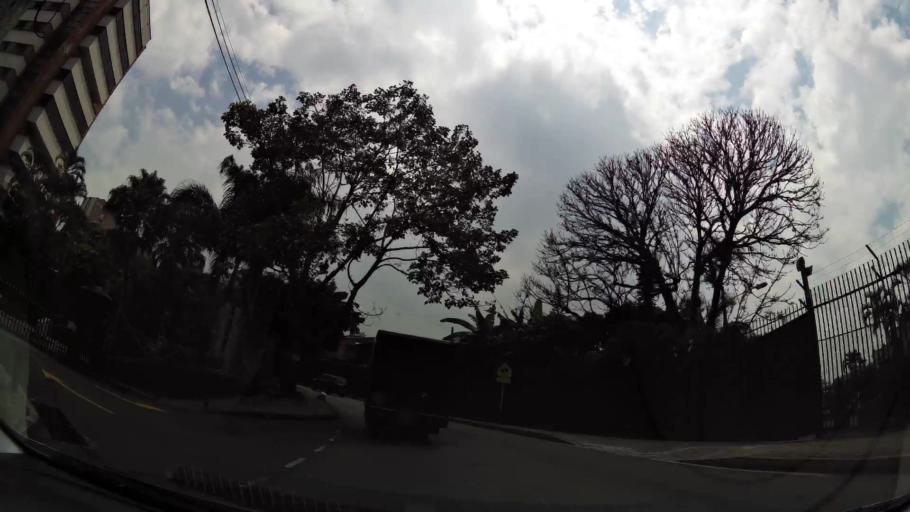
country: CO
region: Antioquia
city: Envigado
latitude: 6.1918
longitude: -75.5696
